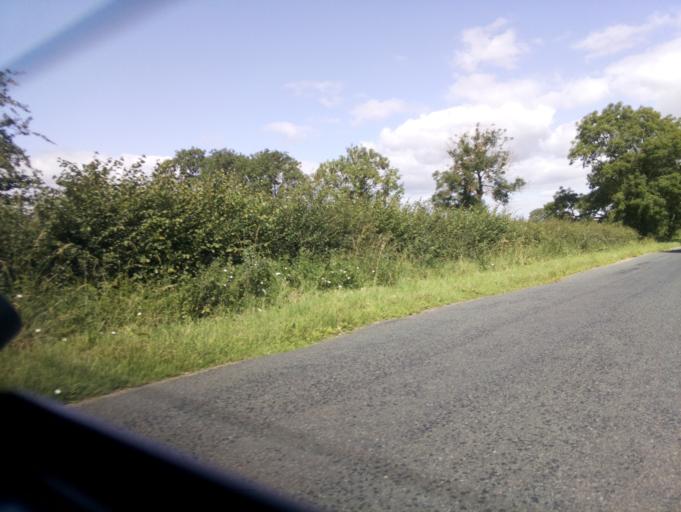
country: GB
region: England
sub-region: Milton Keynes
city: Calverton
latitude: 51.9934
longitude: -0.8601
